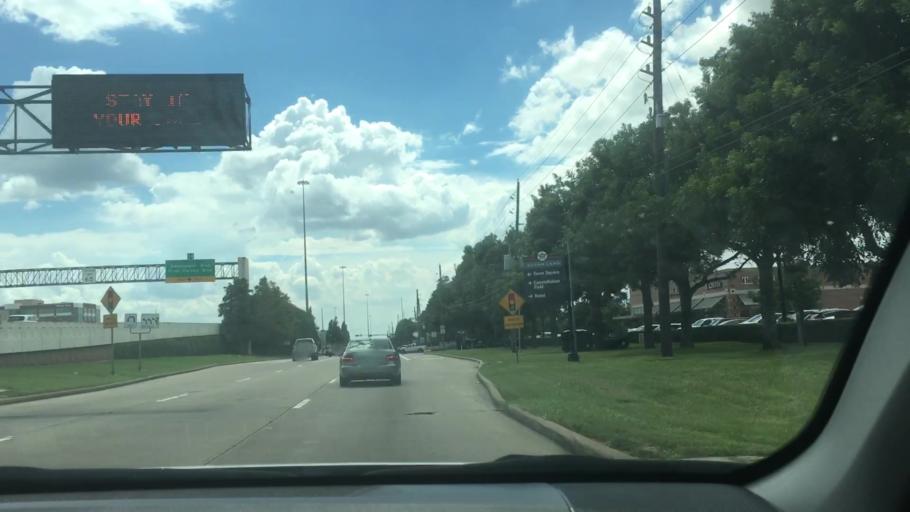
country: US
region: Texas
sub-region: Fort Bend County
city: Sugar Land
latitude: 29.6007
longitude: -95.6208
